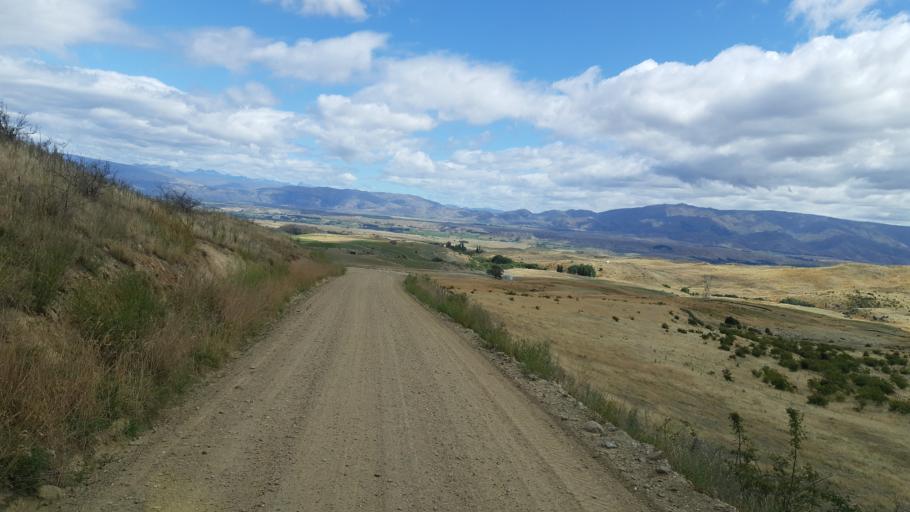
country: NZ
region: Otago
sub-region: Queenstown-Lakes District
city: Wanaka
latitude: -45.2172
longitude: 169.5676
